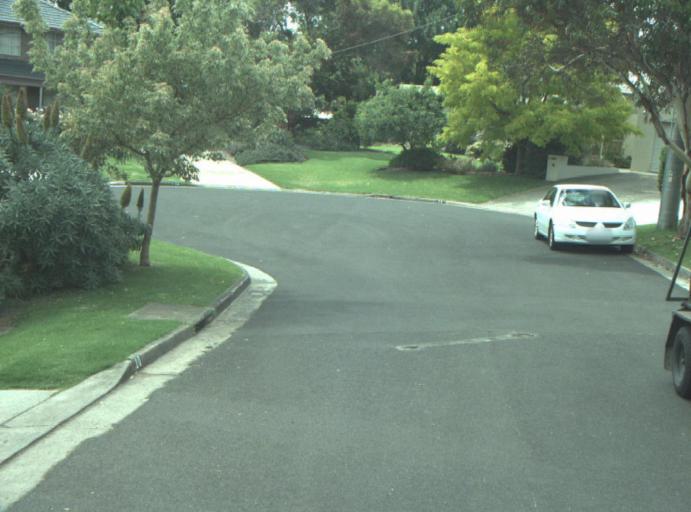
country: AU
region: Victoria
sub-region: Greater Geelong
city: Geelong West
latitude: -38.1673
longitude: 144.3360
